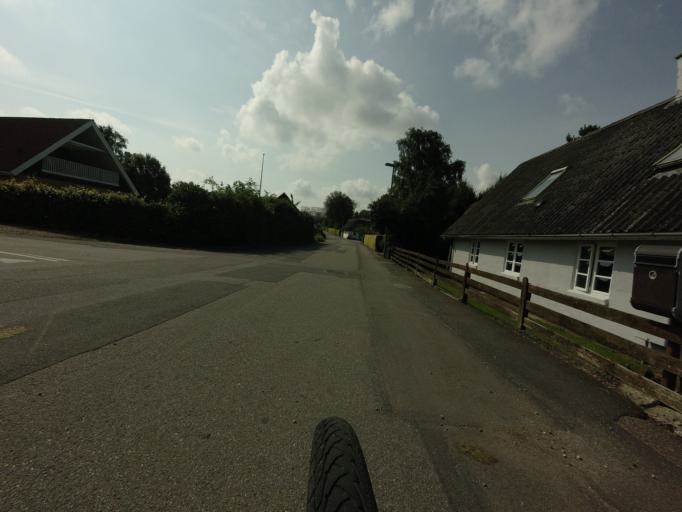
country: DK
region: Zealand
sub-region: Naestved Kommune
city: Naestved
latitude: 55.2191
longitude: 11.8119
